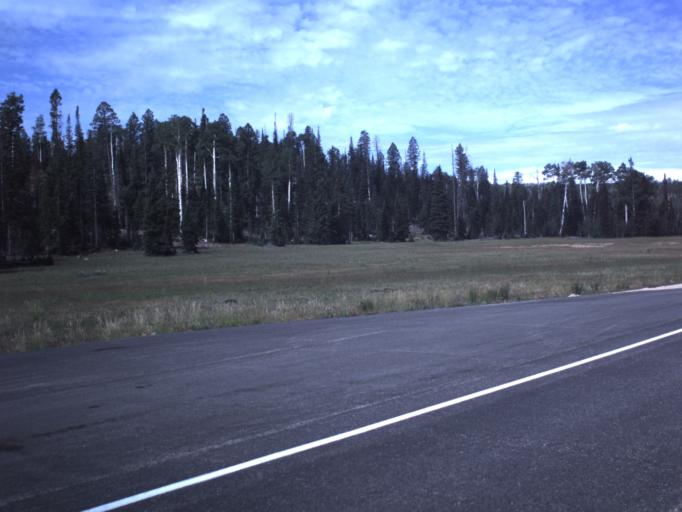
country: US
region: Utah
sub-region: Iron County
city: Parowan
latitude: 37.5413
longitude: -112.7818
